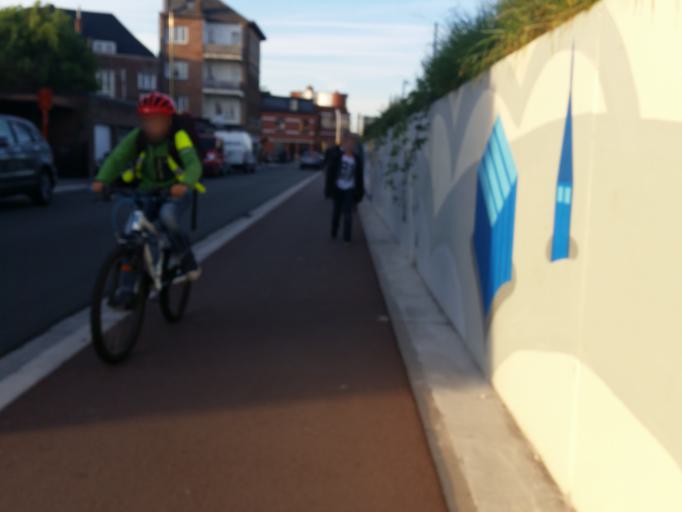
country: BE
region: Flanders
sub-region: Provincie Vlaams-Brabant
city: Vilvoorde
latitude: 50.9289
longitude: 4.4358
